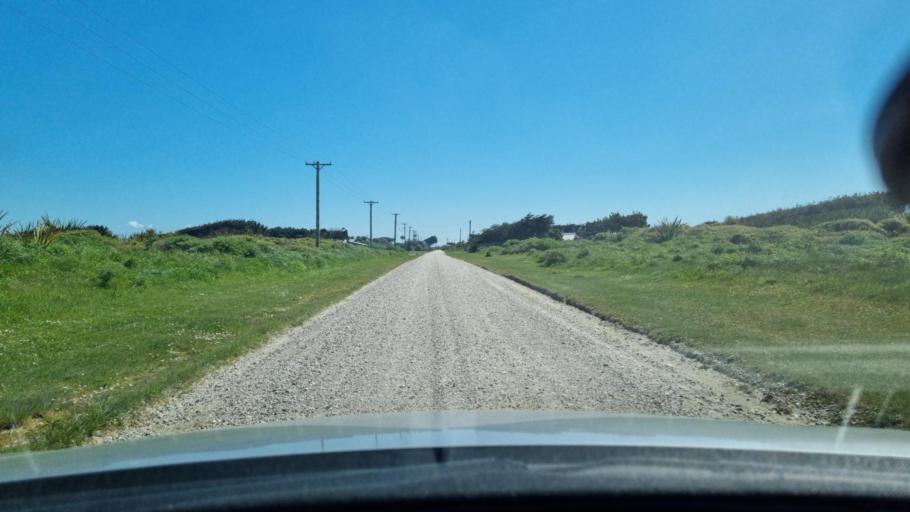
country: NZ
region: Southland
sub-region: Invercargill City
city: Invercargill
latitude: -46.4327
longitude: 168.2351
